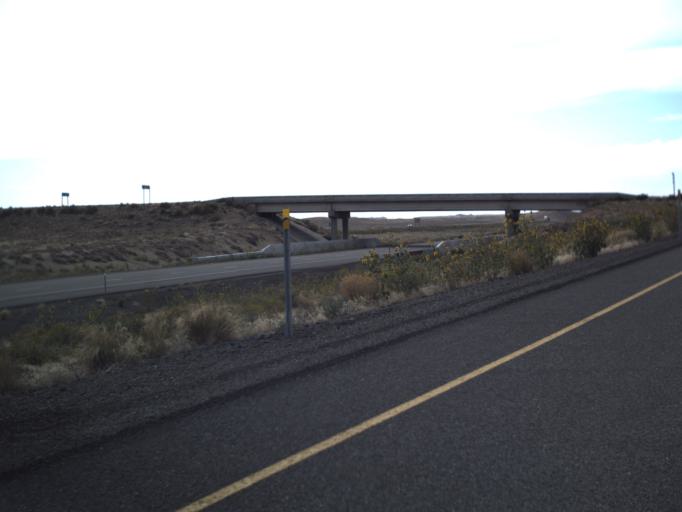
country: US
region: Utah
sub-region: Grand County
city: Moab
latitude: 38.9431
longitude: -109.6125
